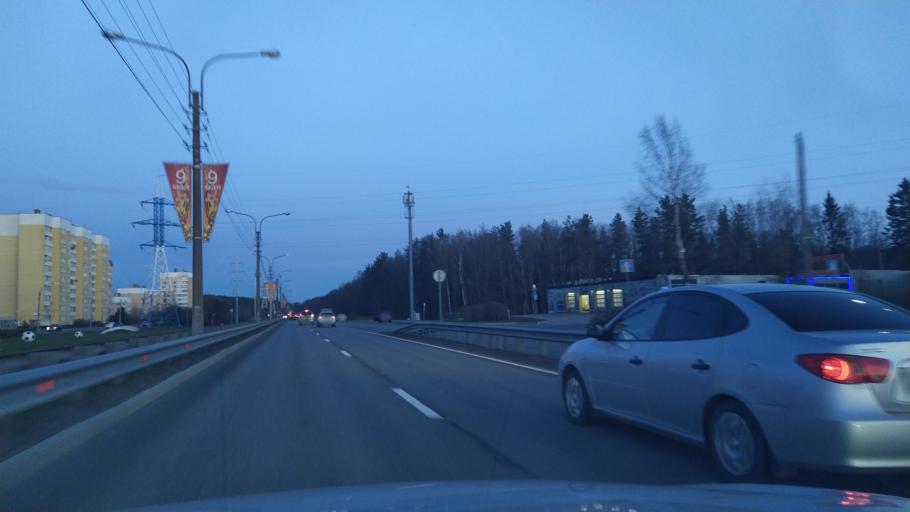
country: RU
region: St.-Petersburg
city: Razliv
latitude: 60.0807
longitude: 29.9599
